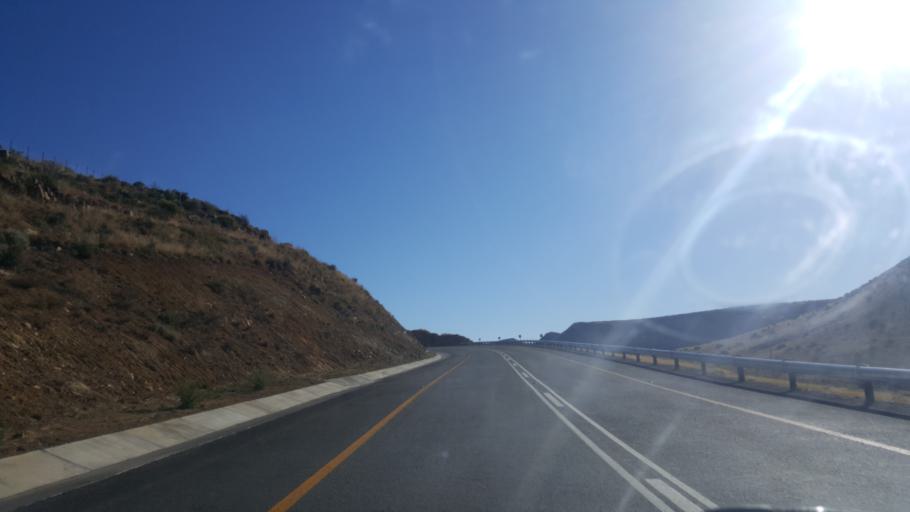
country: ZA
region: Eastern Cape
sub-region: Chris Hani District Municipality
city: Middelburg
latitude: -31.3817
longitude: 25.0331
